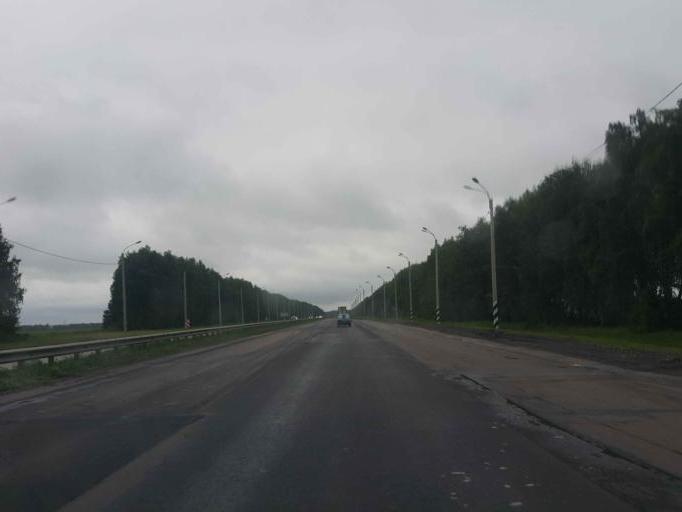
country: RU
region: Tambov
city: Selezni
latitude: 52.7604
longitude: 41.1332
